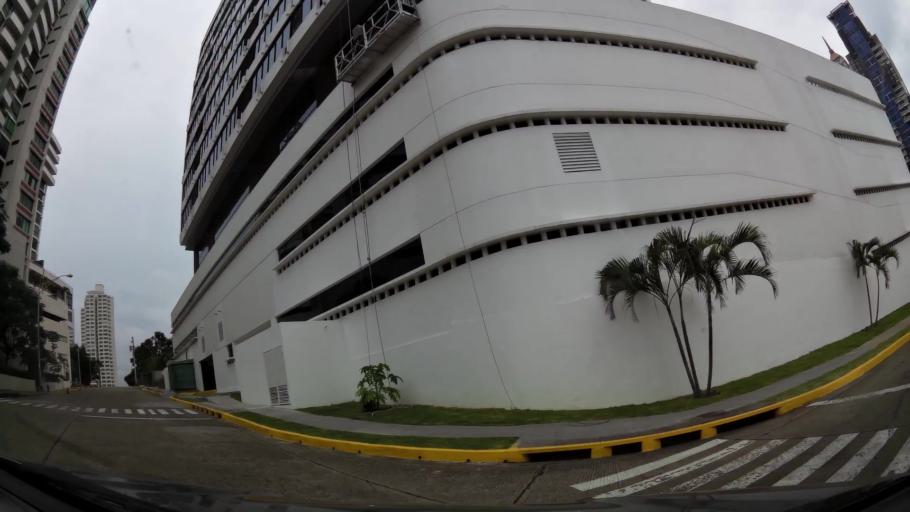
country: PA
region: Panama
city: Panama
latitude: 8.9918
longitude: -79.5316
